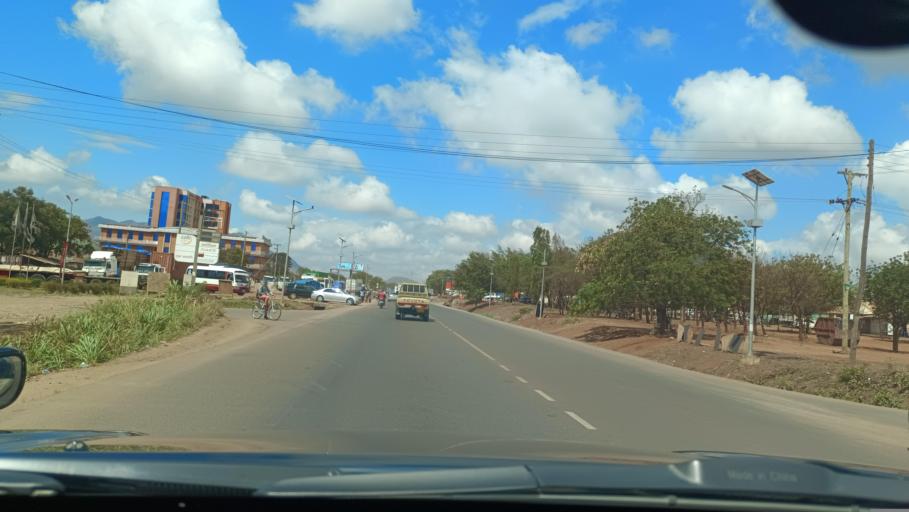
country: TZ
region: Morogoro
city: Morogoro
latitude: -6.8048
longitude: 37.6683
